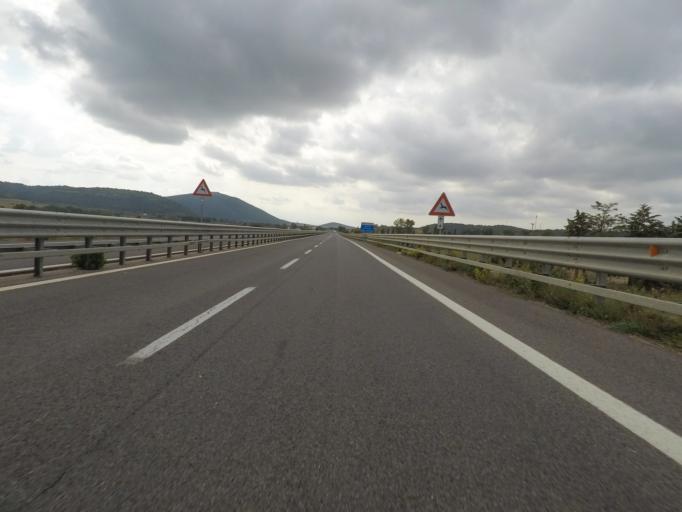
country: IT
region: Tuscany
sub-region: Provincia di Grosseto
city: Bagno Roselle
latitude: 42.8483
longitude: 11.1569
